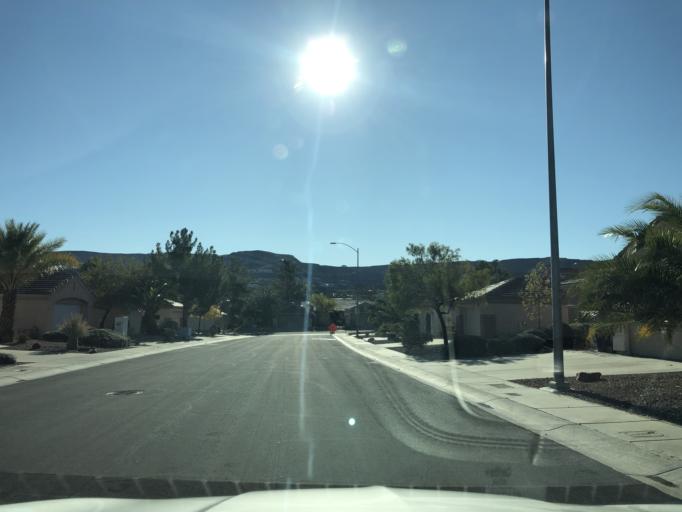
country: US
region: Nevada
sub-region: Clark County
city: Whitney
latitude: 36.0082
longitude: -115.0695
